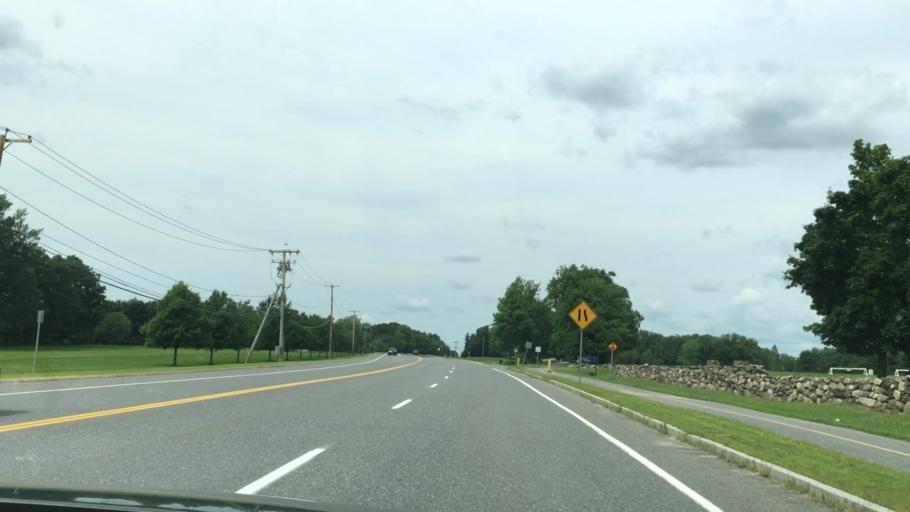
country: US
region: Massachusetts
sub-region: Worcester County
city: Gardner
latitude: 42.5933
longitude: -71.9869
